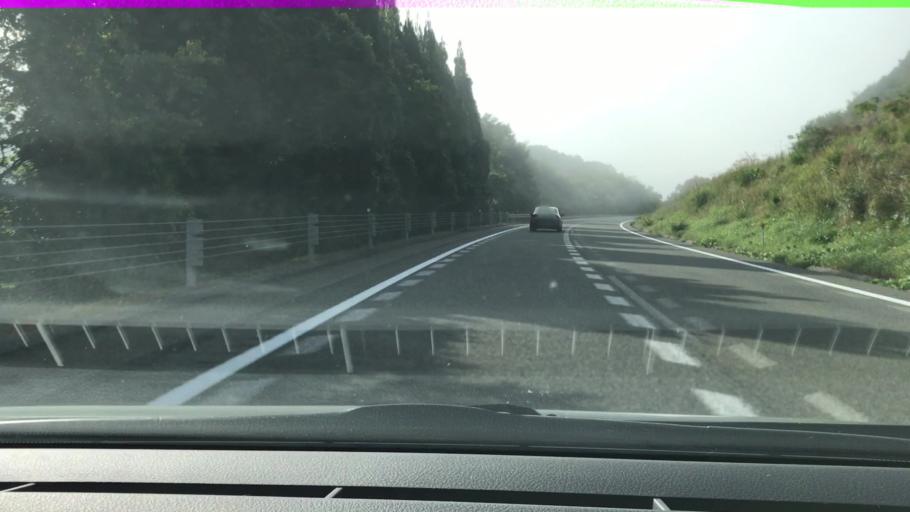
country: JP
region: Hyogo
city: Sasayama
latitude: 35.1050
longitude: 135.1706
